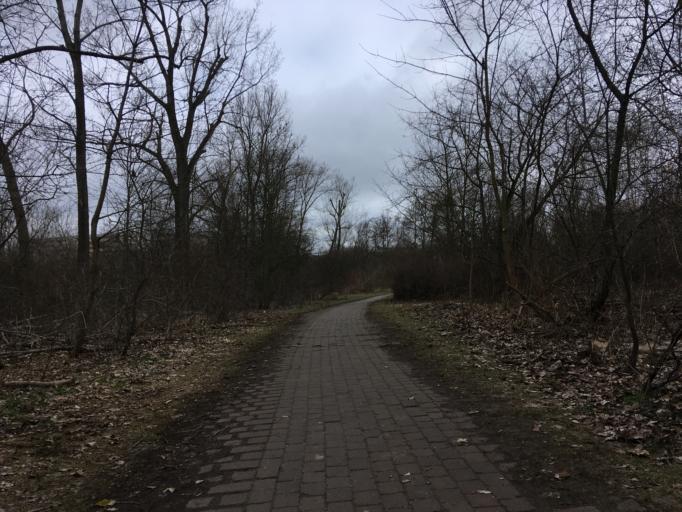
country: DE
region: Berlin
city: Falkenberg
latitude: 52.5618
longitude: 13.5337
